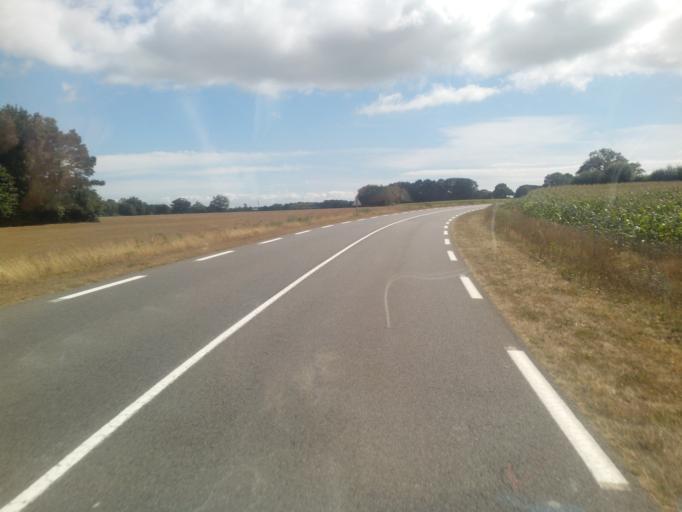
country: FR
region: Brittany
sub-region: Departement du Morbihan
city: Peaule
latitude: 47.5903
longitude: -2.3755
